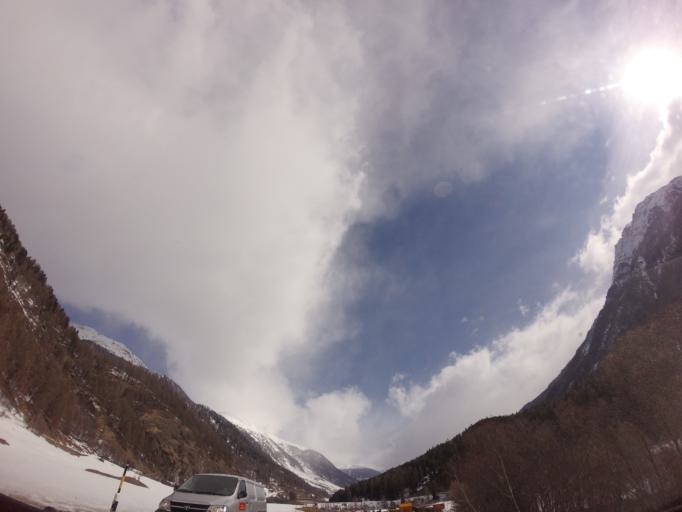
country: CH
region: Grisons
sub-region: Inn District
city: Zernez
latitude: 46.7561
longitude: 10.0855
